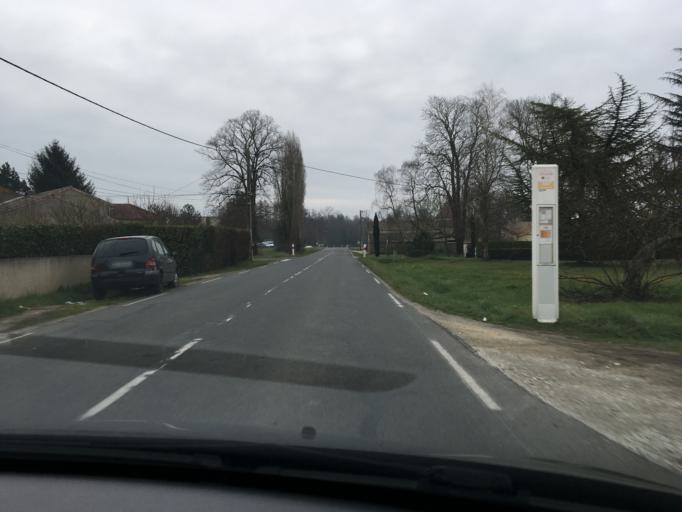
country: FR
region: Aquitaine
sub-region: Departement de la Gironde
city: Saint-Ciers-sur-Gironde
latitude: 45.2728
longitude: -0.5921
